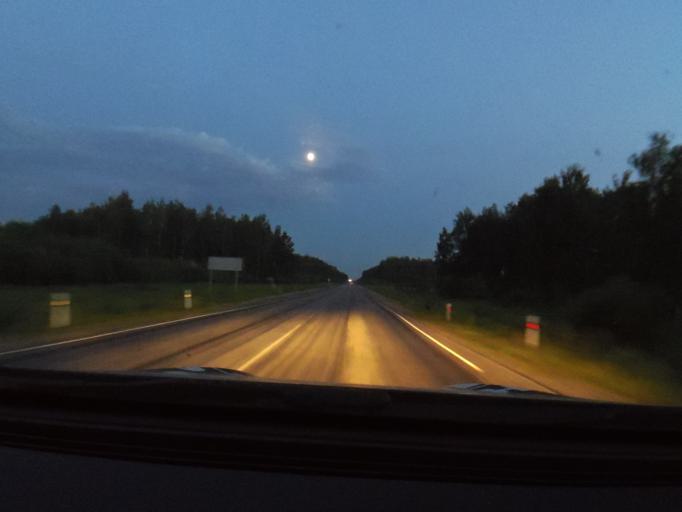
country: RU
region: Bashkortostan
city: Duvan
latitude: 56.0027
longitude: 58.2129
